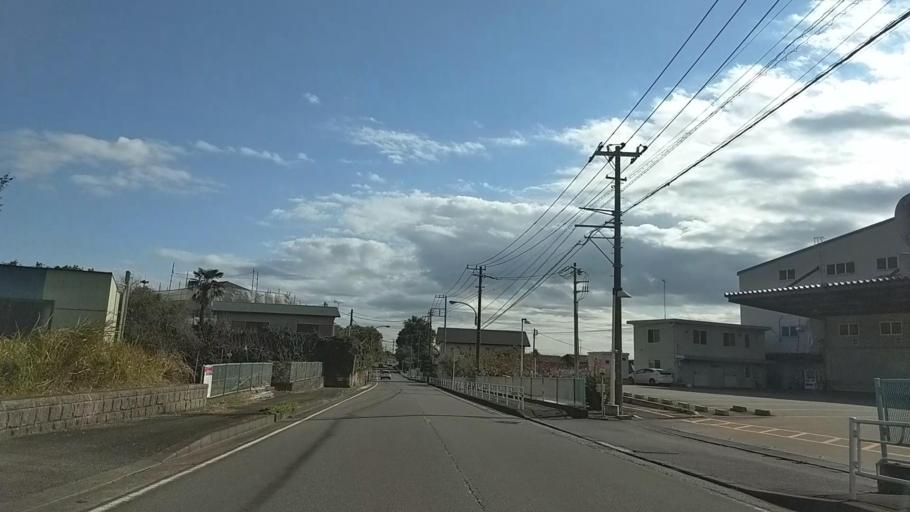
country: JP
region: Kanagawa
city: Odawara
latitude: 35.3119
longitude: 139.1766
